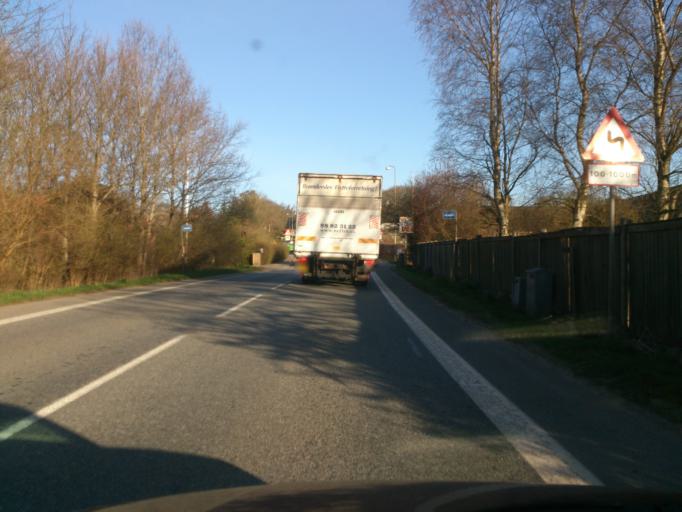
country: DK
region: Central Jutland
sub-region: Favrskov Kommune
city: Ulstrup
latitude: 56.4505
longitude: 9.7253
